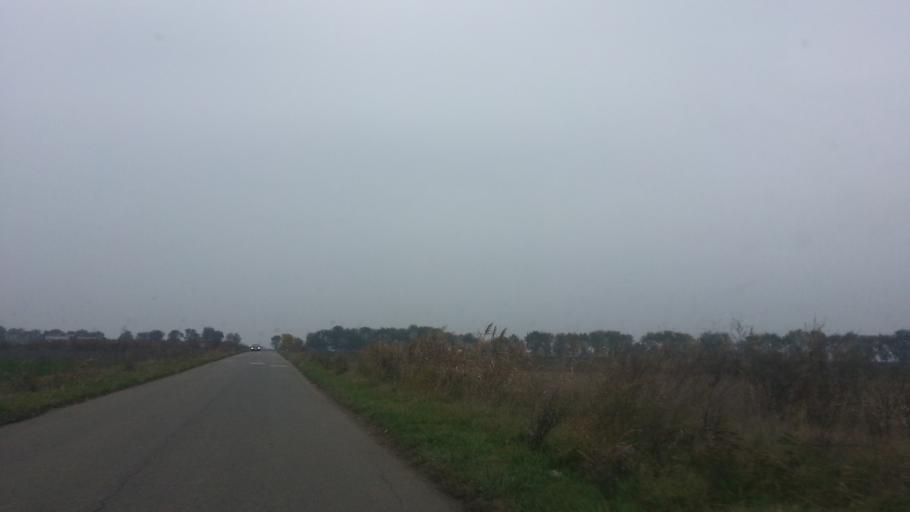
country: RS
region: Autonomna Pokrajina Vojvodina
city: Nova Pazova
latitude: 44.9582
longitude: 20.2166
